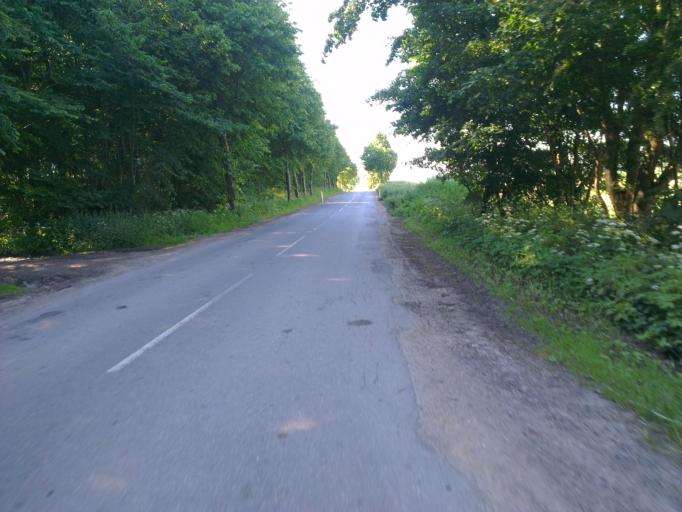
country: DK
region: Capital Region
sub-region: Frederikssund Kommune
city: Skibby
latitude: 55.7811
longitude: 11.9425
